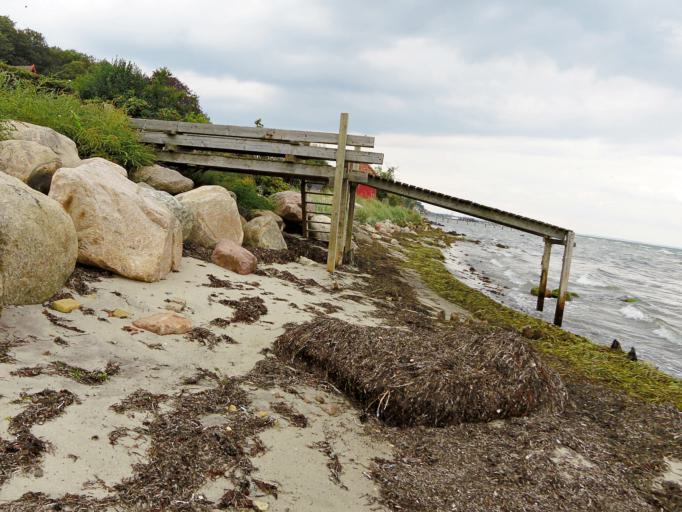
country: DK
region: Capital Region
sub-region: Fredensborg Kommune
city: Humlebaek
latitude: 55.9468
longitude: 12.5300
